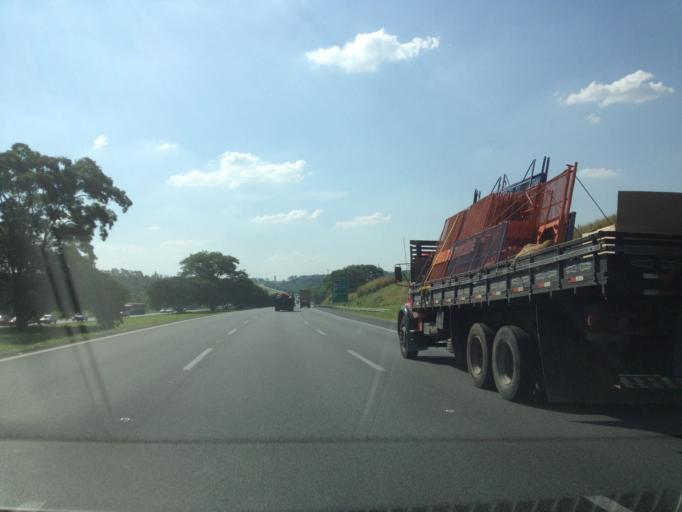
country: BR
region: Sao Paulo
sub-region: Valinhos
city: Valinhos
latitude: -23.0090
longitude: -47.0921
